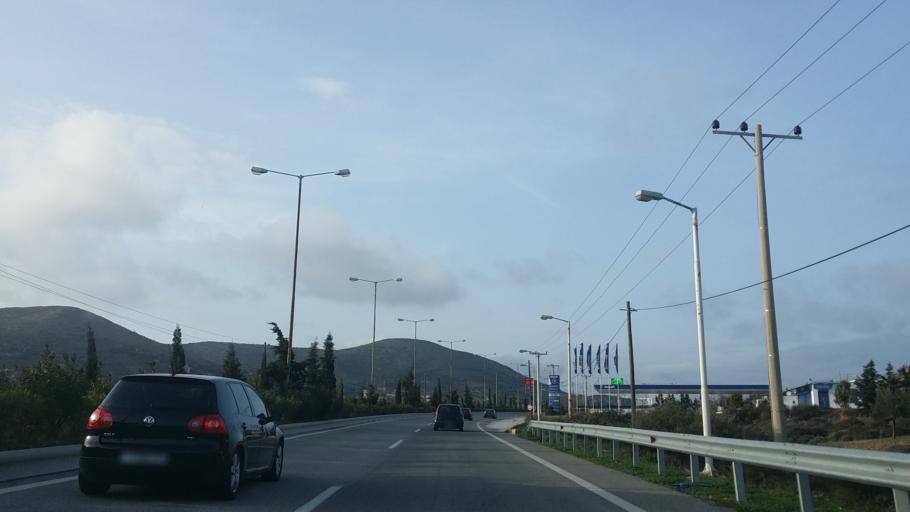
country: GR
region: Attica
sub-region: Nomarchia Anatolikis Attikis
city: Lavrio
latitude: 37.7702
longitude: 24.0545
